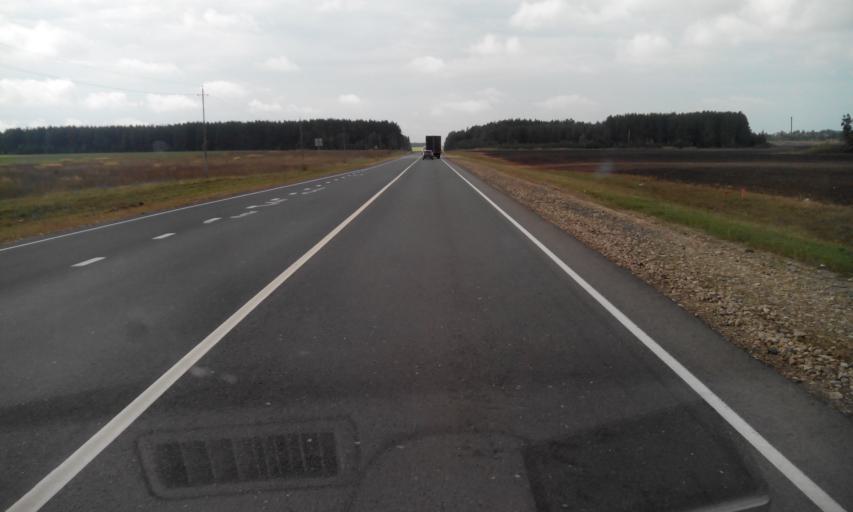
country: RU
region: Penza
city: Kuznetsk
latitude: 53.0916
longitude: 46.6891
